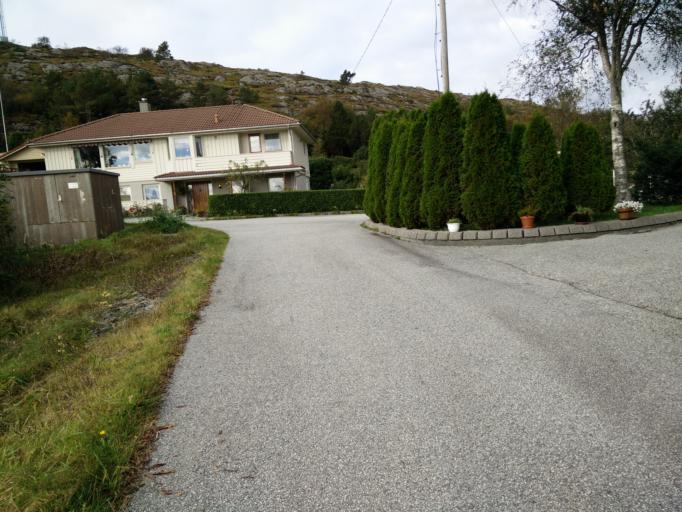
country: NO
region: Hordaland
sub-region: Sveio
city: Sveio
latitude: 59.6062
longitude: 5.2117
